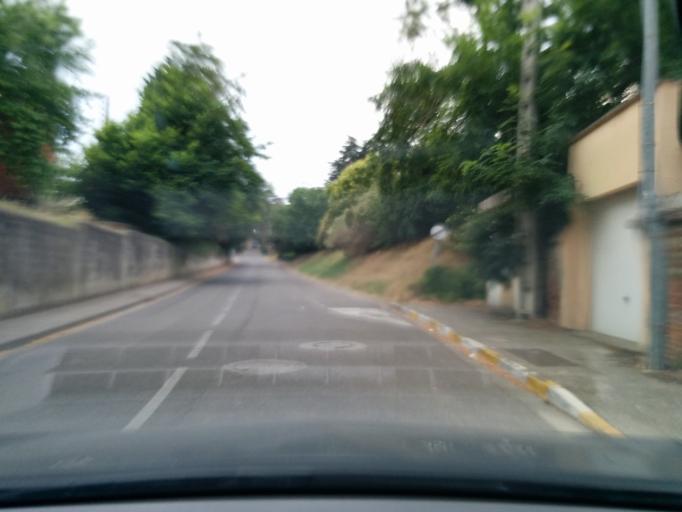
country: FR
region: Midi-Pyrenees
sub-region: Departement de la Haute-Garonne
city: Castanet-Tolosan
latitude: 43.5170
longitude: 1.4974
